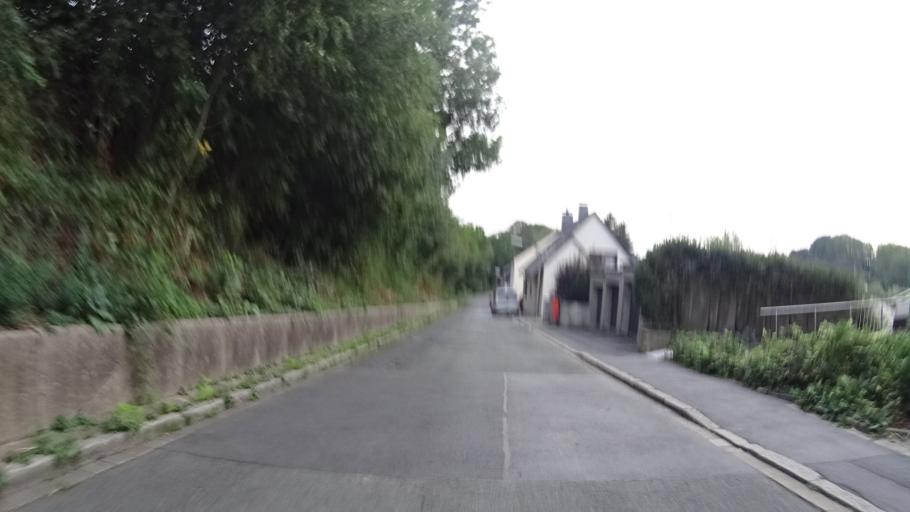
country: DE
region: North Rhine-Westphalia
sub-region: Regierungsbezirk Arnsberg
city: Dortmund
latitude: 51.4934
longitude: 7.4399
